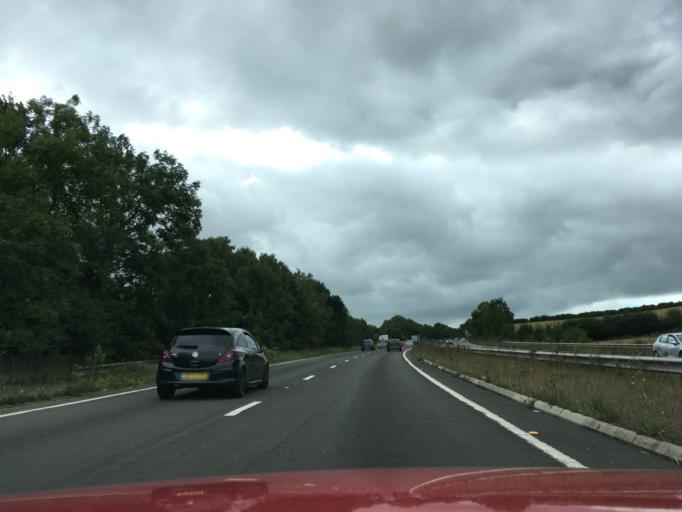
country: GB
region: England
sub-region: Devon
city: Kingskerswell
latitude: 50.4820
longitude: -3.5764
